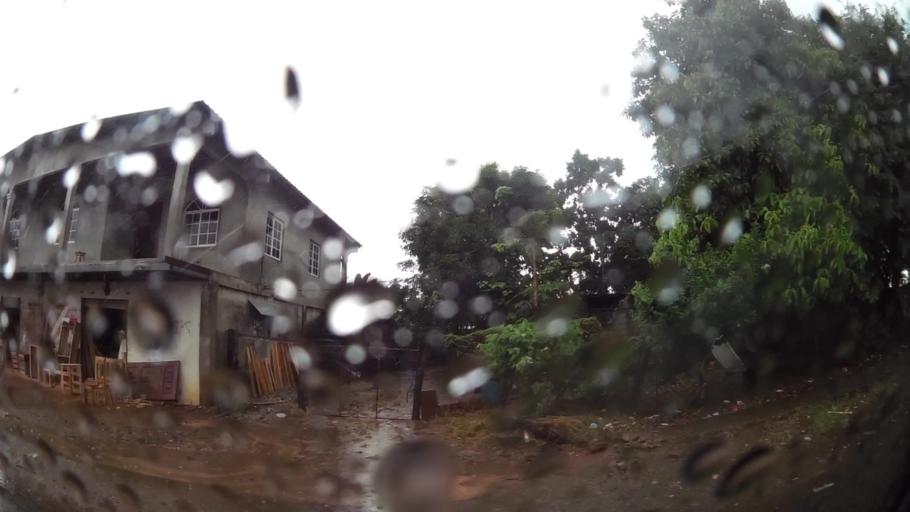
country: PA
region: Panama
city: Cabra Numero Uno
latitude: 9.1029
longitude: -79.3314
